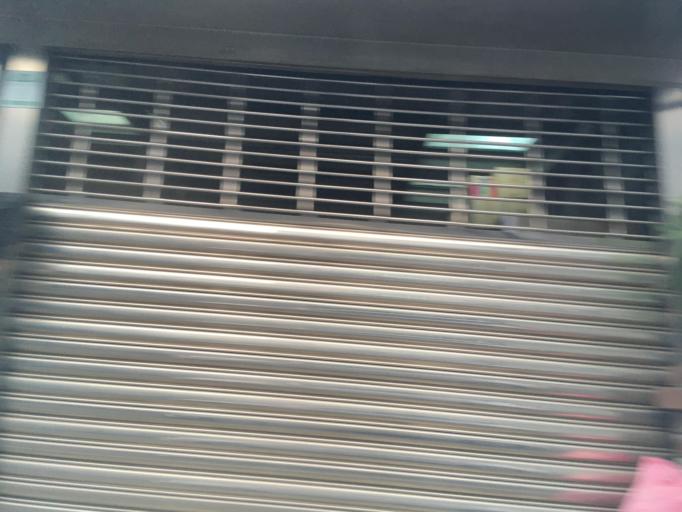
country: TW
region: Taiwan
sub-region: Yilan
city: Yilan
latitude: 24.7489
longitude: 121.7252
